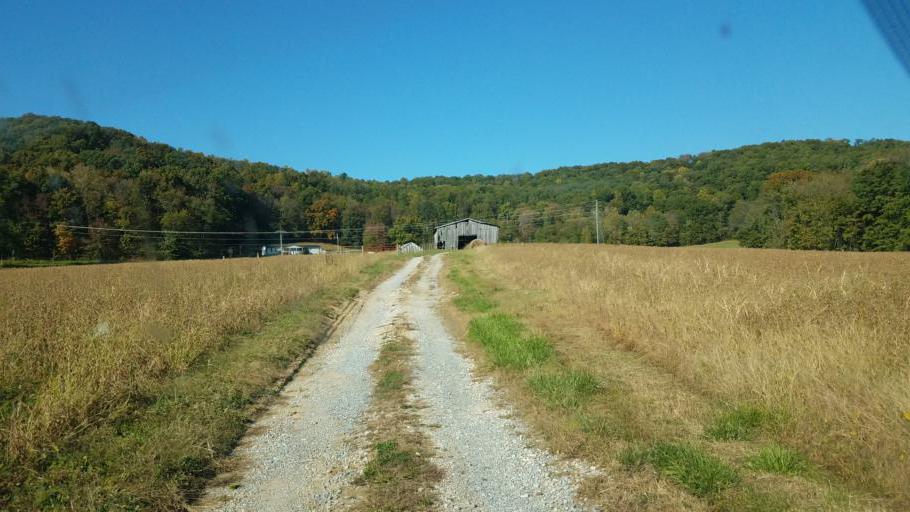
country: US
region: Kentucky
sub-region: Fleming County
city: Flemingsburg
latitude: 38.4660
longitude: -83.5611
